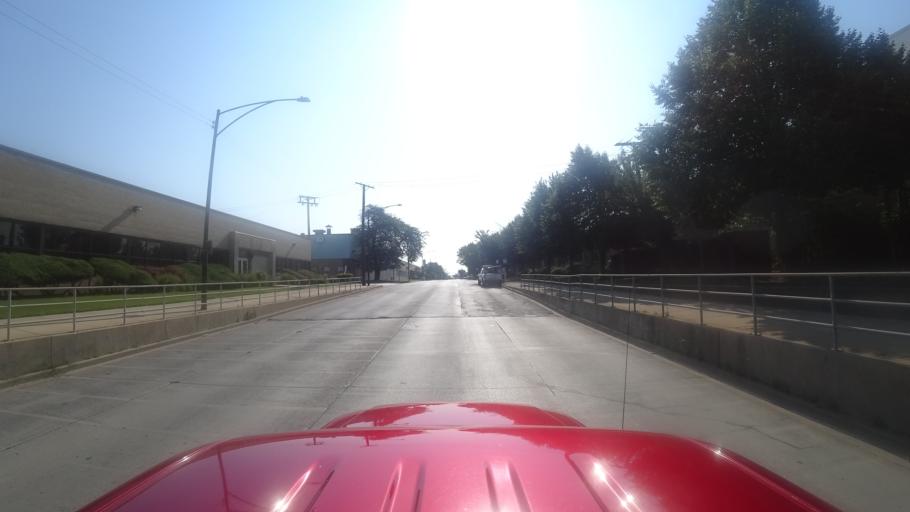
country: US
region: Illinois
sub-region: Cook County
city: Cicero
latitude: 41.8077
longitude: -87.7377
